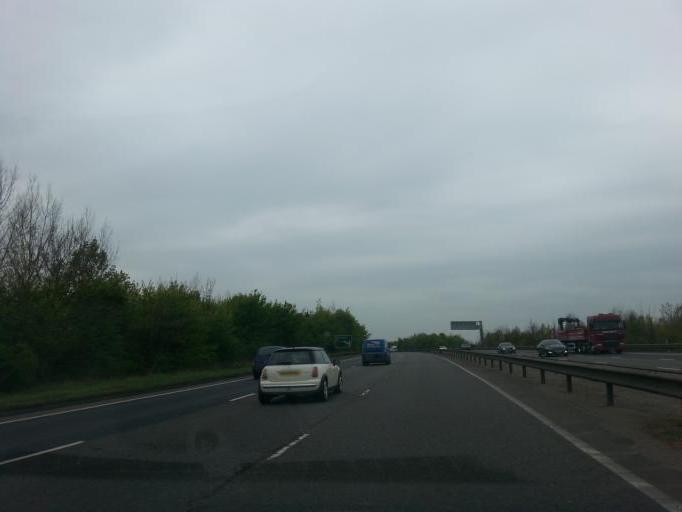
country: GB
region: England
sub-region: Suffolk
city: Newmarket
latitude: 52.2684
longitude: 0.4160
